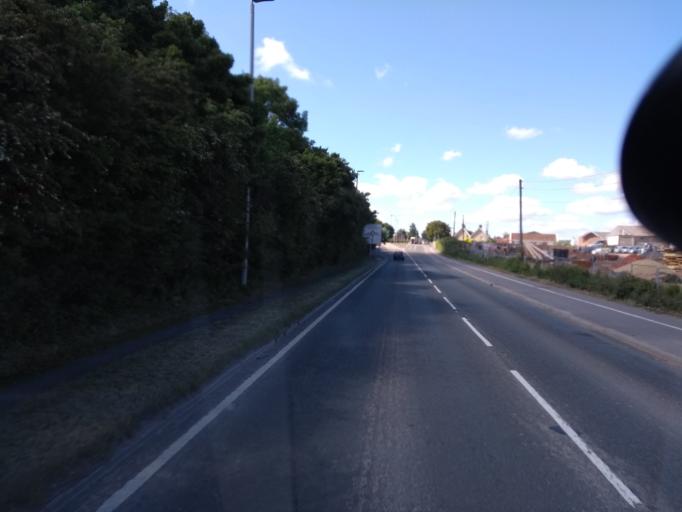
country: GB
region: England
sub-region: Somerset
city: Bridgwater
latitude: 51.1060
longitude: -2.9956
